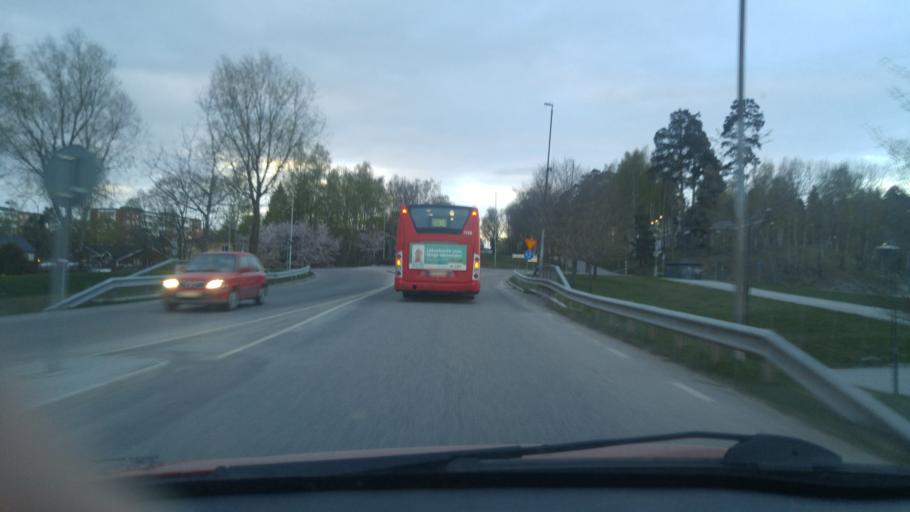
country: SE
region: Stockholm
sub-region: Upplands Vasby Kommun
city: Upplands Vaesby
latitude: 59.5182
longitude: 17.9183
